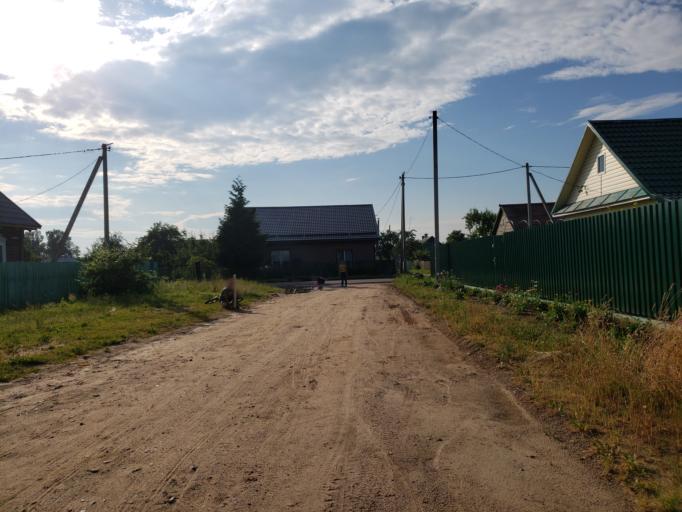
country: BY
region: Minsk
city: Chervyen'
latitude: 53.7031
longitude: 28.4426
